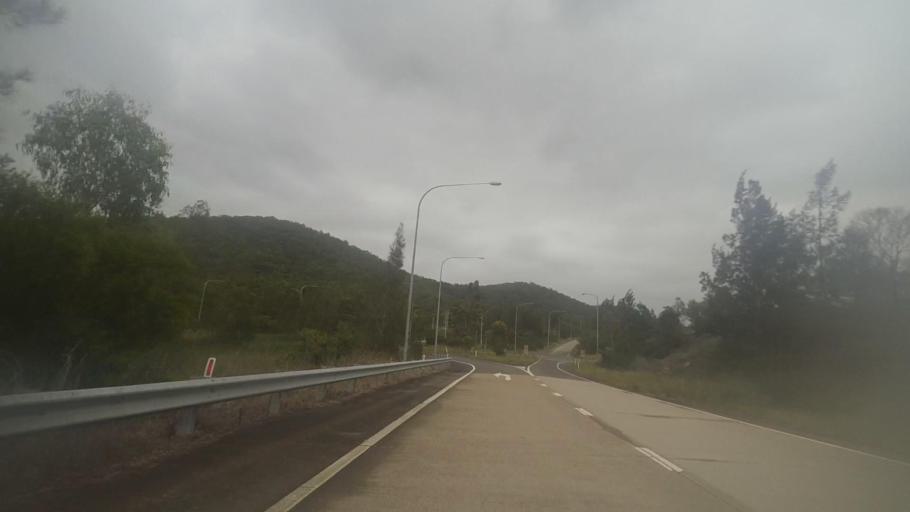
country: AU
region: New South Wales
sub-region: Port Stephens Shire
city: Port Stephens
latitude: -32.6327
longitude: 151.9969
